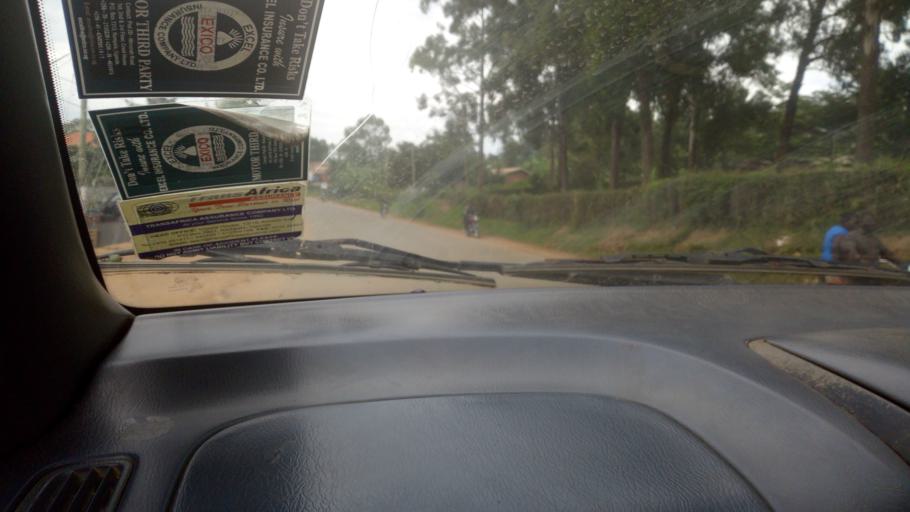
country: UG
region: Western Region
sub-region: Mbarara District
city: Mbarara
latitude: -0.6038
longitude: 30.6523
